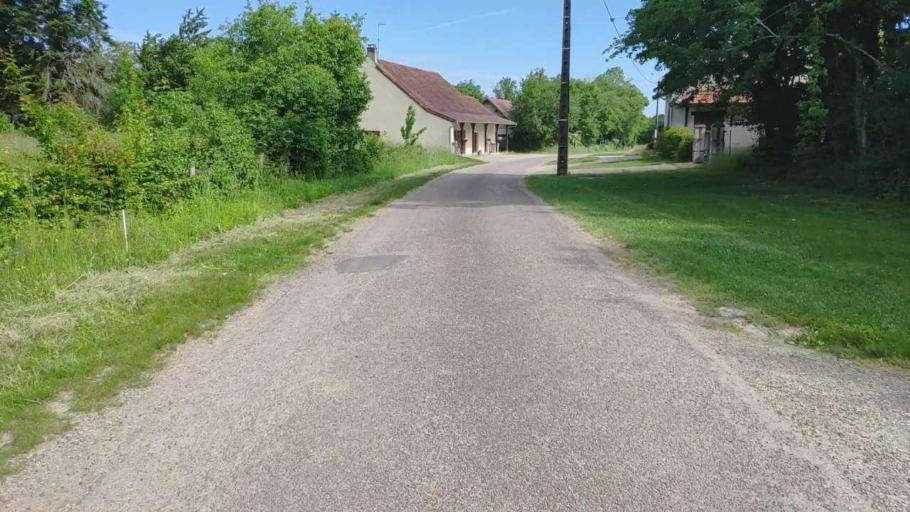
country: FR
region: Franche-Comte
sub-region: Departement du Jura
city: Bletterans
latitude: 46.7126
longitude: 5.4447
